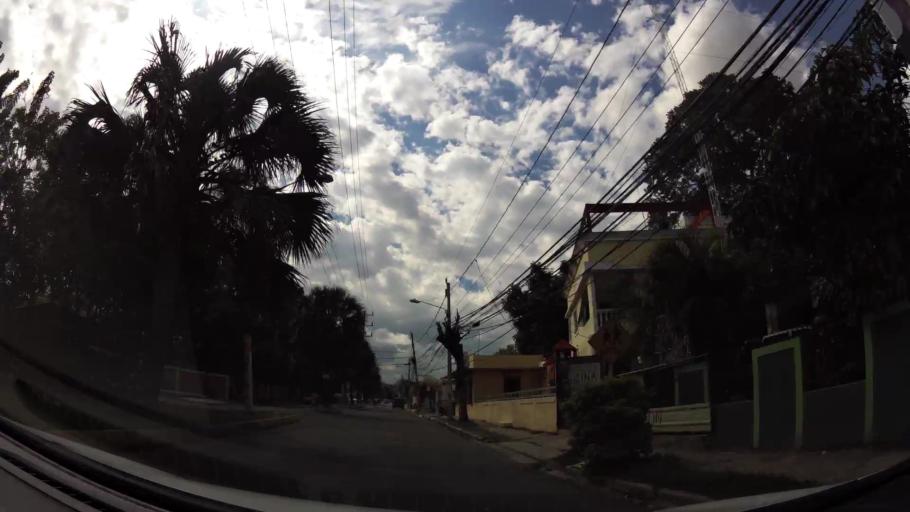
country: DO
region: La Vega
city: Concepcion de La Vega
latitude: 19.2197
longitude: -70.5274
